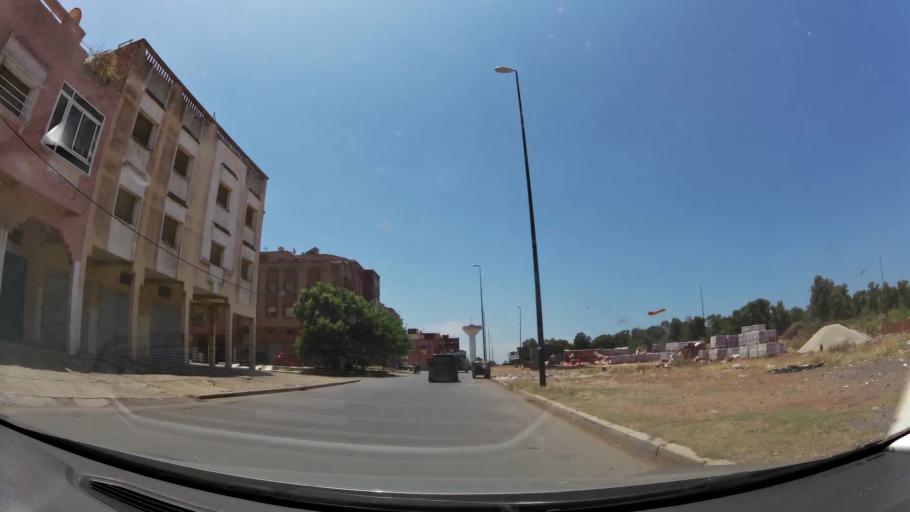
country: MA
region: Gharb-Chrarda-Beni Hssen
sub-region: Kenitra Province
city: Kenitra
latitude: 34.2584
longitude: -6.6267
